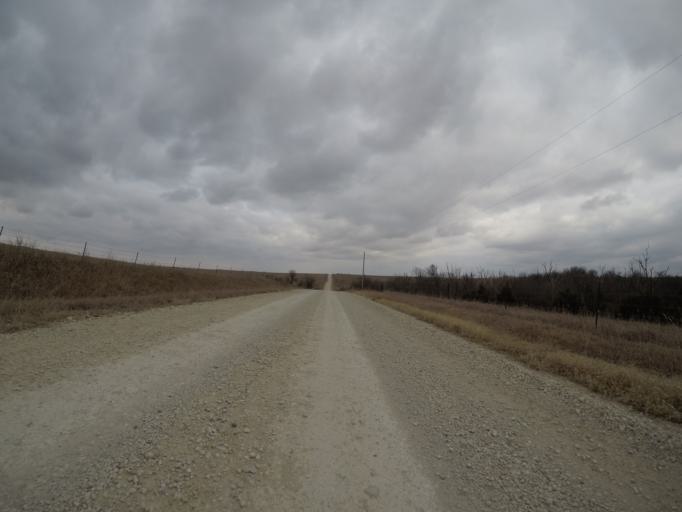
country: US
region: Kansas
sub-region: Morris County
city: Council Grove
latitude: 38.7504
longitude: -96.2795
